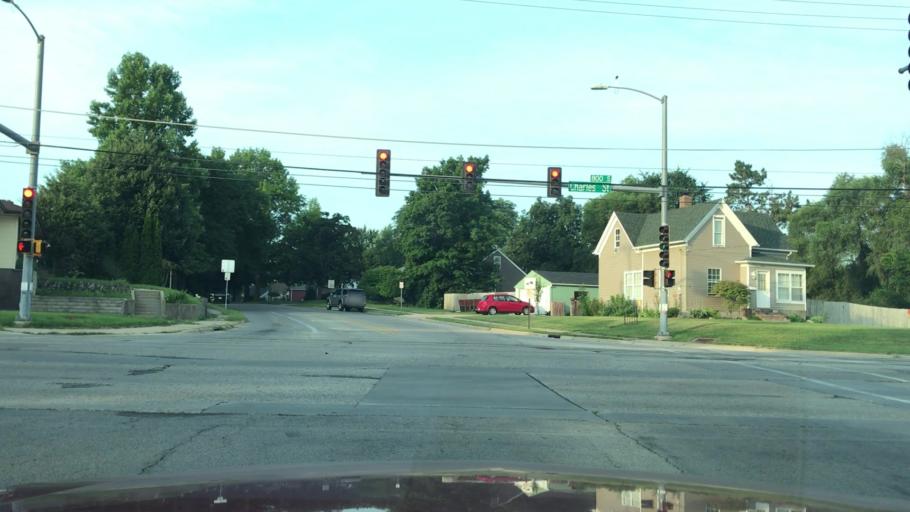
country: US
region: Illinois
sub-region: Winnebago County
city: Rockford
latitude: 42.2566
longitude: -89.0431
